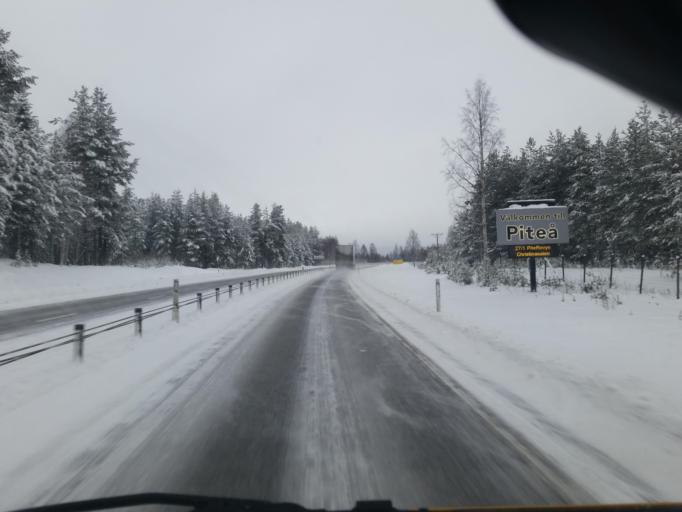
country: SE
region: Norrbotten
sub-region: Pitea Kommun
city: Bergsviken
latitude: 65.3051
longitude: 21.4101
